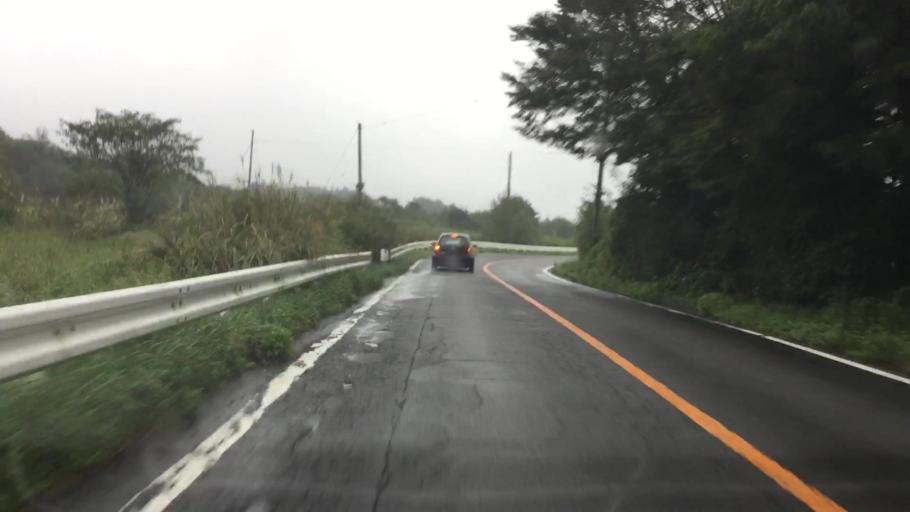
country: JP
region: Yamanashi
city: Fujikawaguchiko
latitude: 35.4123
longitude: 138.6201
